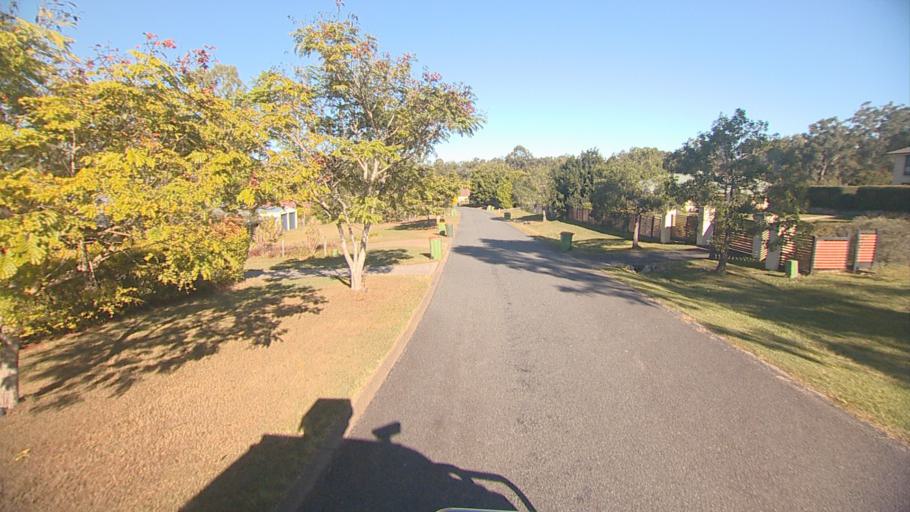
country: AU
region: Queensland
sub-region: Logan
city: North Maclean
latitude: -27.7430
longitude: 152.9595
